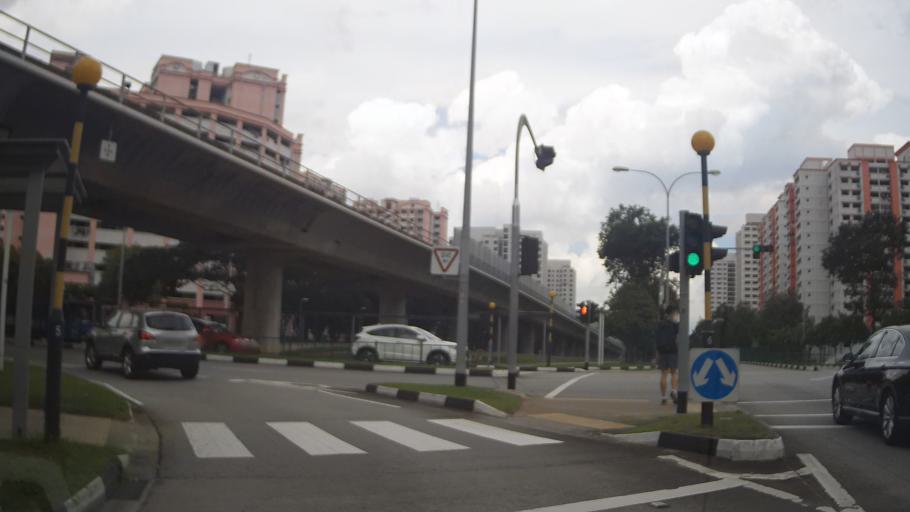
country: MY
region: Johor
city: Johor Bahru
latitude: 1.4003
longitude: 103.7487
